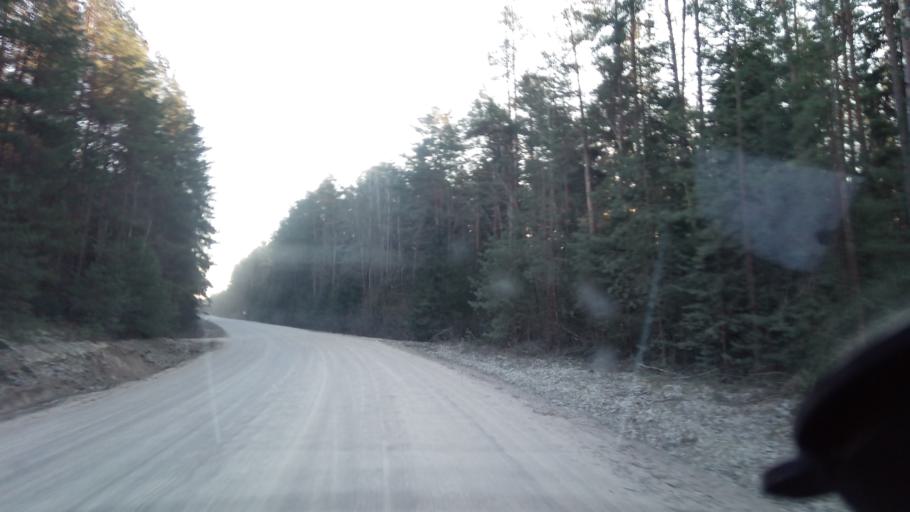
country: LT
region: Alytaus apskritis
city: Druskininkai
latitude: 54.1469
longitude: 23.9387
